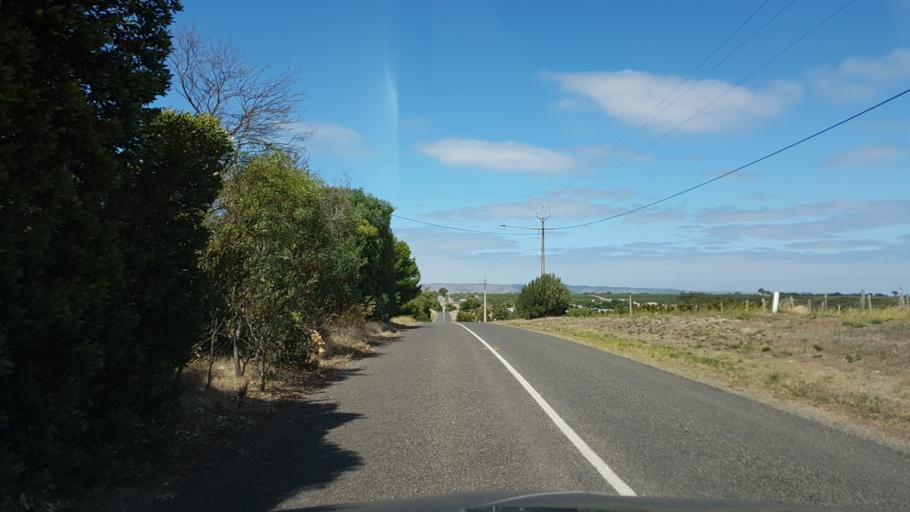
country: AU
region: South Australia
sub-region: Onkaparinga
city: McLaren Vale
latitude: -35.2142
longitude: 138.5176
